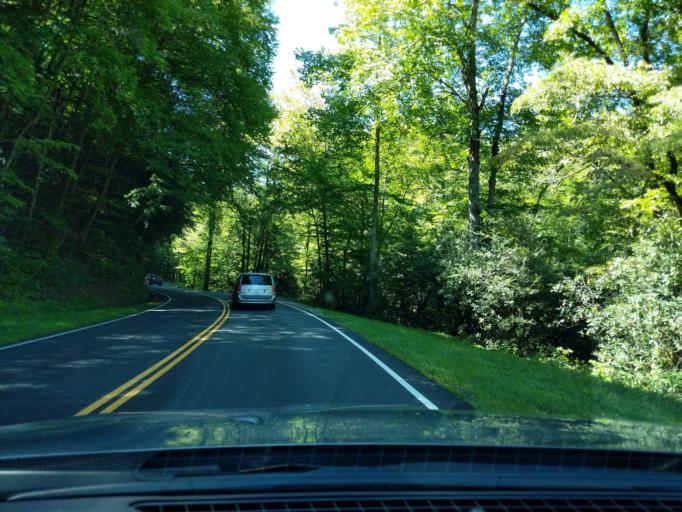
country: US
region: North Carolina
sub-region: Swain County
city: Cherokee
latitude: 35.5435
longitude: -83.3011
